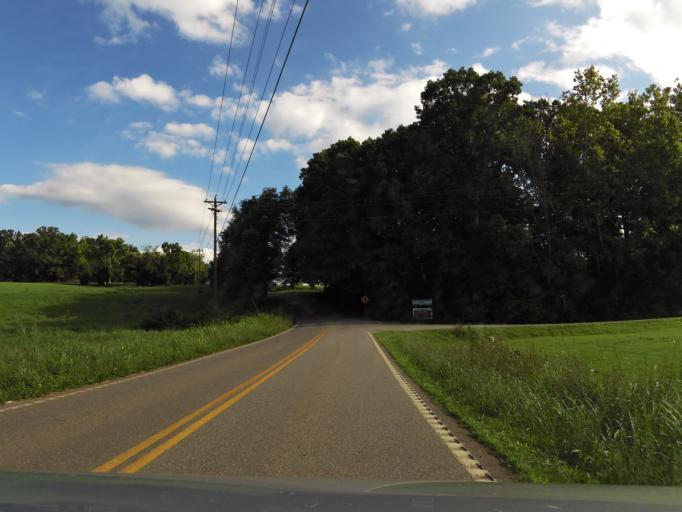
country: US
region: Tennessee
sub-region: Loudon County
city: Greenback
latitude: 35.6367
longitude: -84.0997
